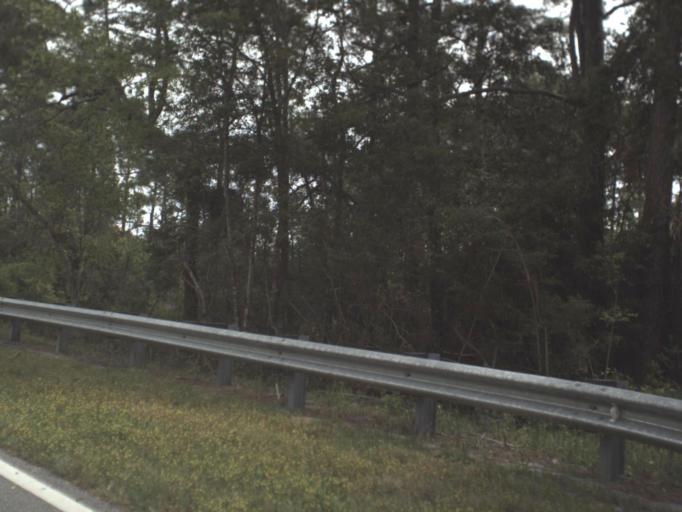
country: US
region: Florida
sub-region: Escambia County
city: Myrtle Grove
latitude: 30.3245
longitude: -87.4165
